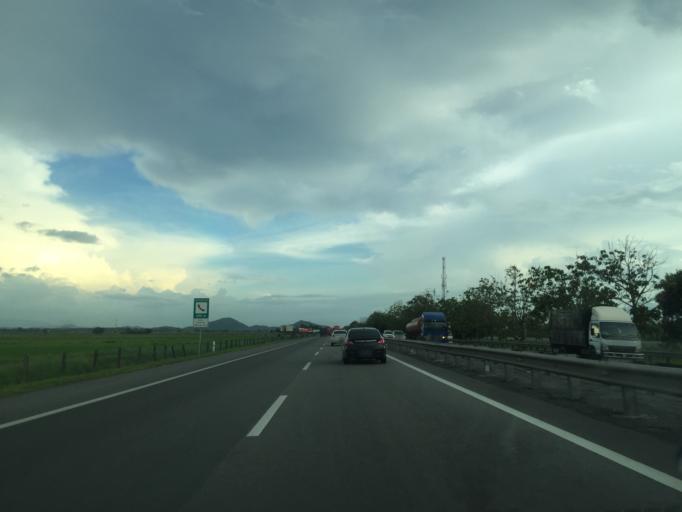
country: MY
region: Kedah
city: Alor Setar
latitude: 5.9953
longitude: 100.4281
